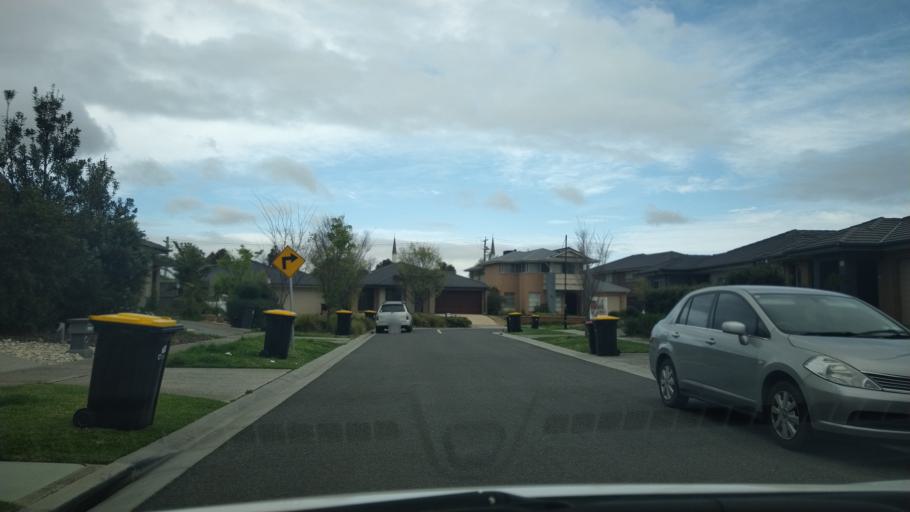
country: AU
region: Victoria
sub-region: Greater Dandenong
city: Keysborough
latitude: -38.0099
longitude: 145.1783
